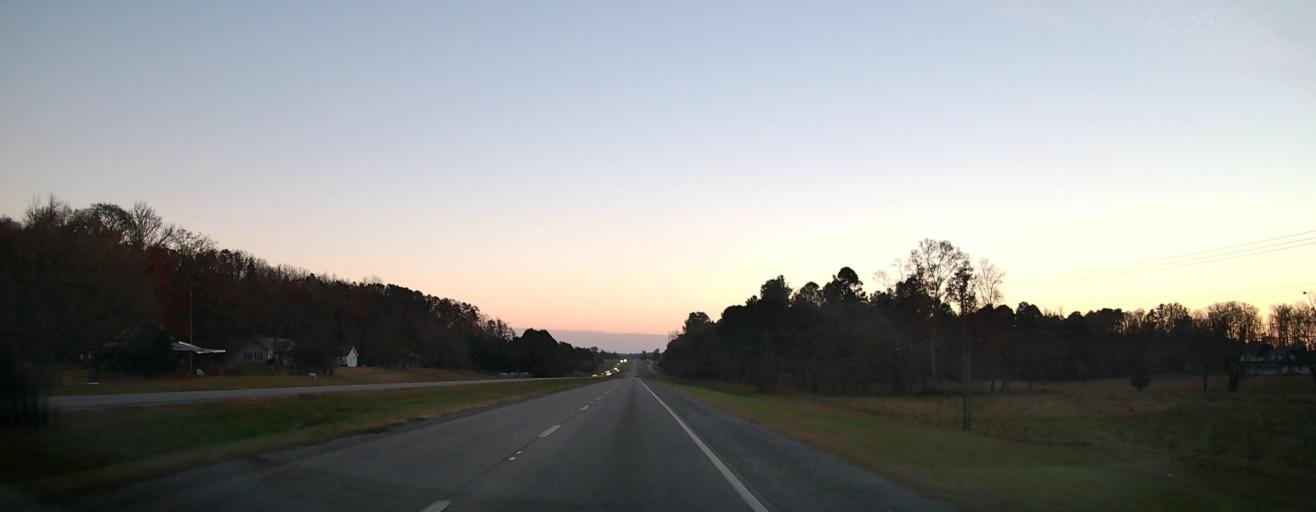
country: US
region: Alabama
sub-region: Calhoun County
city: Alexandria
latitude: 33.8350
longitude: -85.9135
